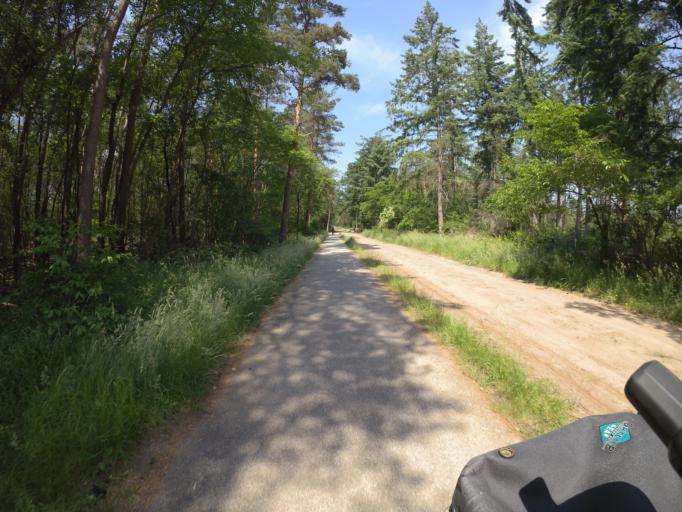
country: NL
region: Overijssel
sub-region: Gemeente Hof van Twente
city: Markelo
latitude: 52.2969
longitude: 6.4567
